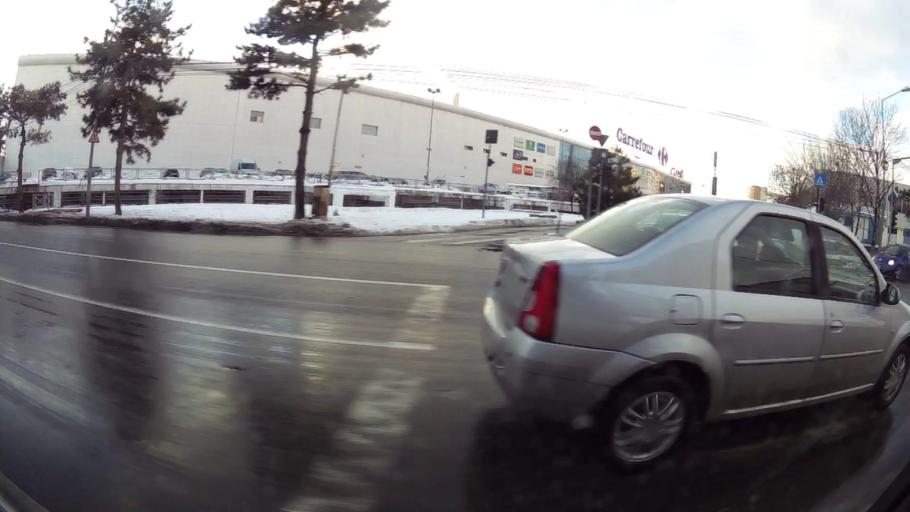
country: RO
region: Ilfov
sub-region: Comuna Popesti-Leordeni
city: Popesti-Leordeni
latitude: 44.3749
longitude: 26.1212
